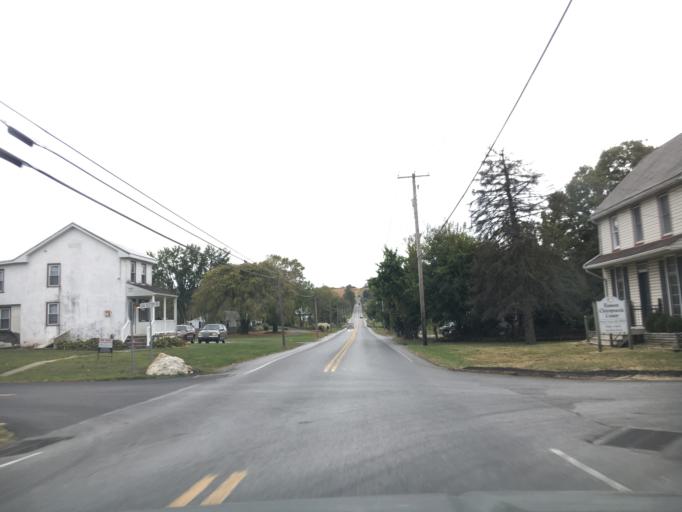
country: US
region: Pennsylvania
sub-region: Lancaster County
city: Quarryville
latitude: 39.8923
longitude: -76.1789
